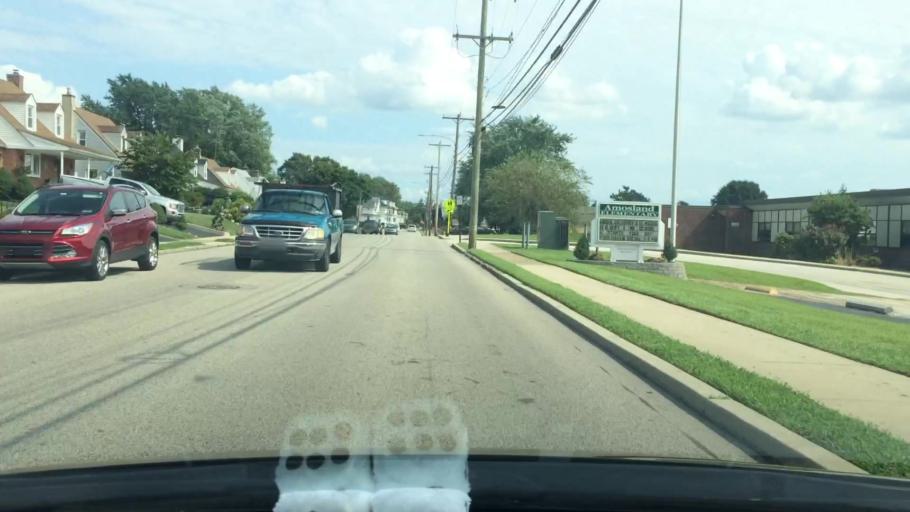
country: US
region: Pennsylvania
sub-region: Delaware County
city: Morton
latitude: 39.9009
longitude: -75.3162
